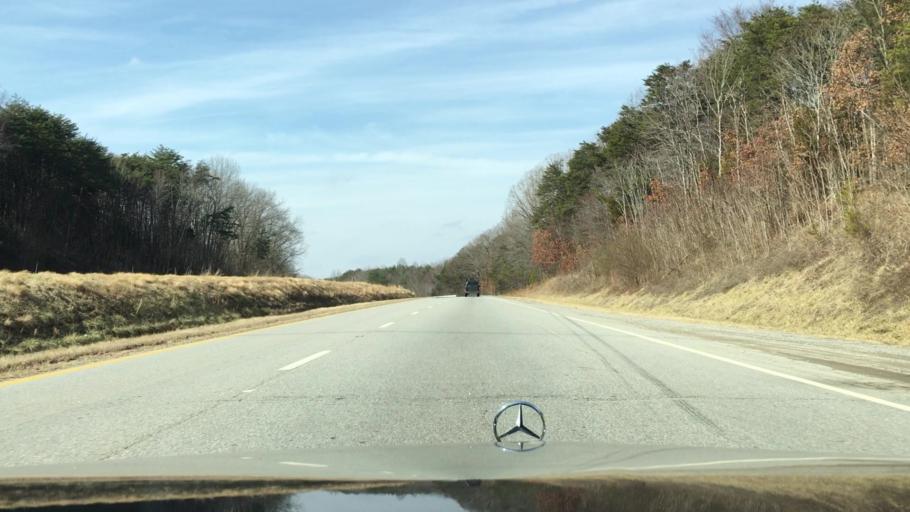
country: US
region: Virginia
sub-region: Prince Edward County
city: Hampden Sydney
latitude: 37.3149
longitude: -78.4662
